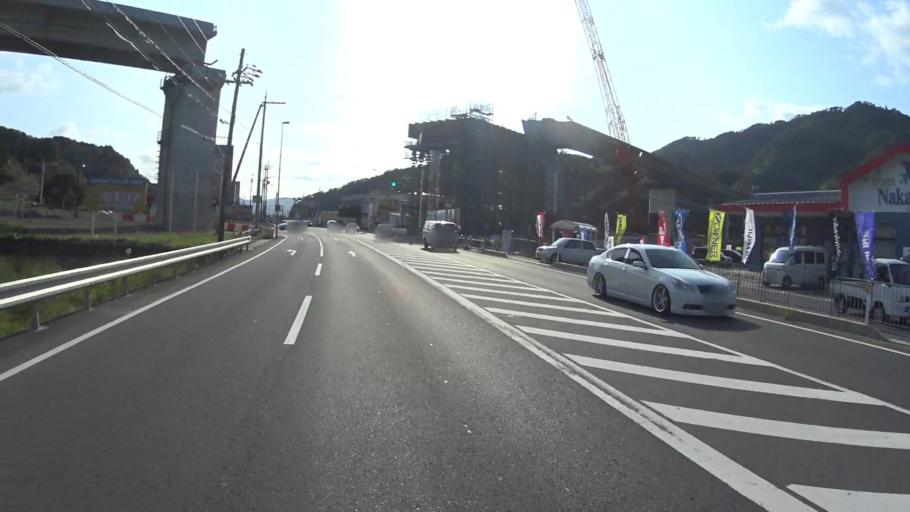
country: JP
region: Kyoto
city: Miyazu
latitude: 35.5517
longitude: 135.1403
